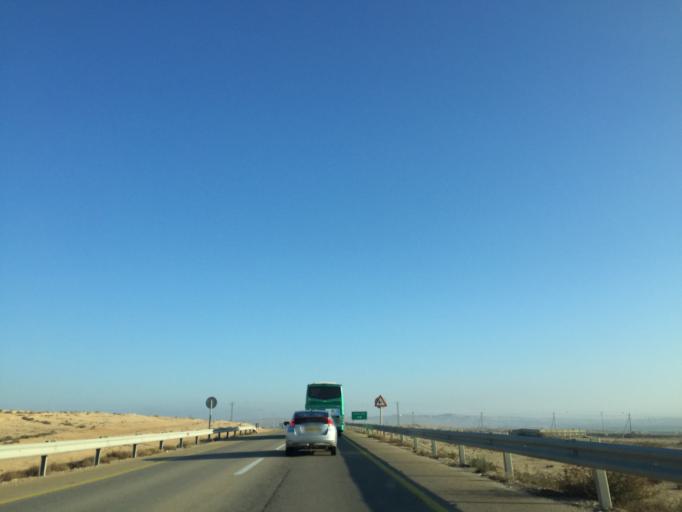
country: IL
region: Southern District
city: Yeroham
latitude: 31.0297
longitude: 34.9714
